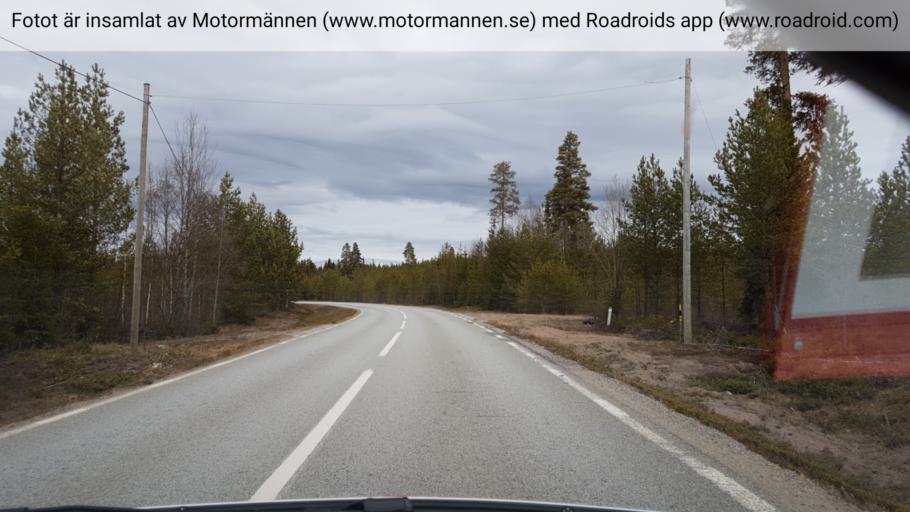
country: SE
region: Vaesterbotten
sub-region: Asele Kommun
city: Asele
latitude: 63.8645
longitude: 17.1730
